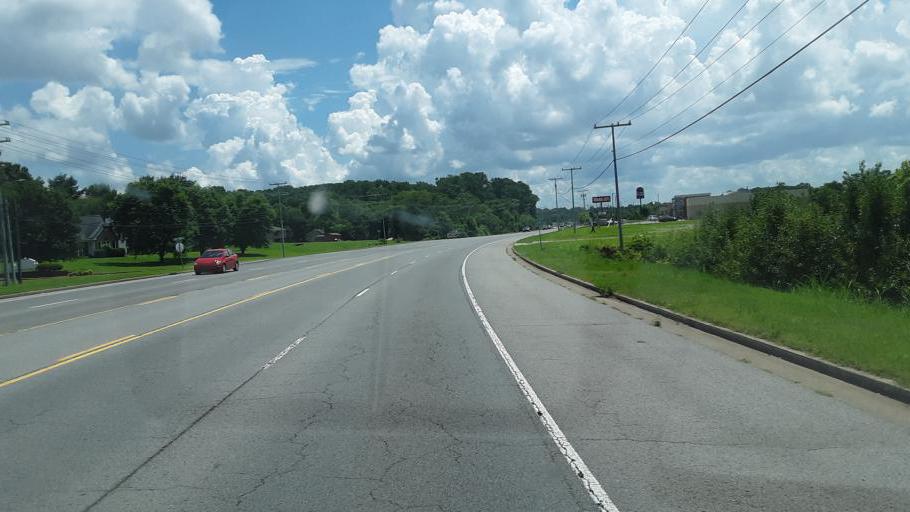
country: US
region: Kentucky
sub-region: Christian County
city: Oak Grove
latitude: 36.6292
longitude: -87.3767
